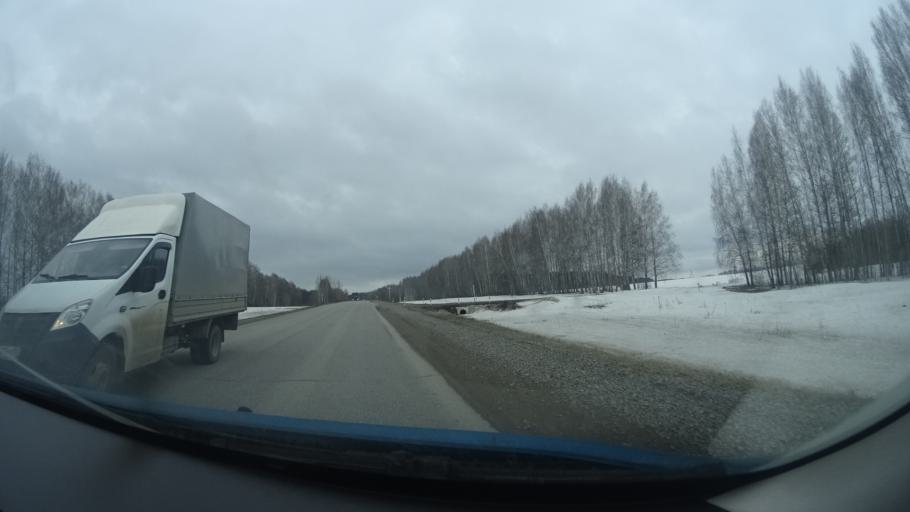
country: RU
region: Bashkortostan
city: Birsk
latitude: 55.3420
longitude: 55.5920
